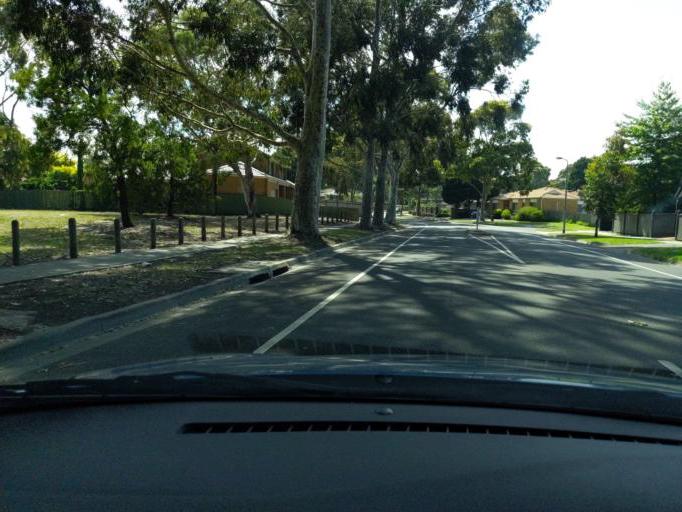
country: AU
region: Victoria
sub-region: Knox
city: Scoresby
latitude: -37.9159
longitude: 145.2431
